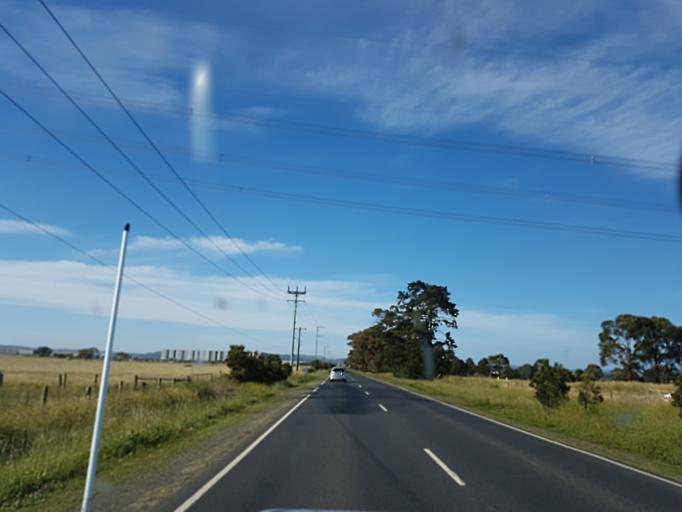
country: AU
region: Victoria
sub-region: Cardinia
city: Pakenham South
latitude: -38.1094
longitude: 145.4866
